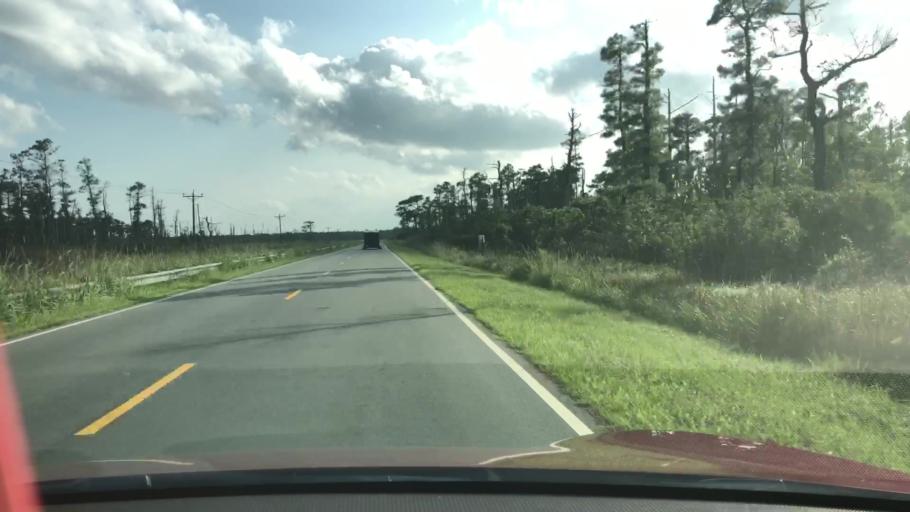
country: US
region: North Carolina
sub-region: Dare County
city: Wanchese
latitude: 35.6165
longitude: -75.7923
